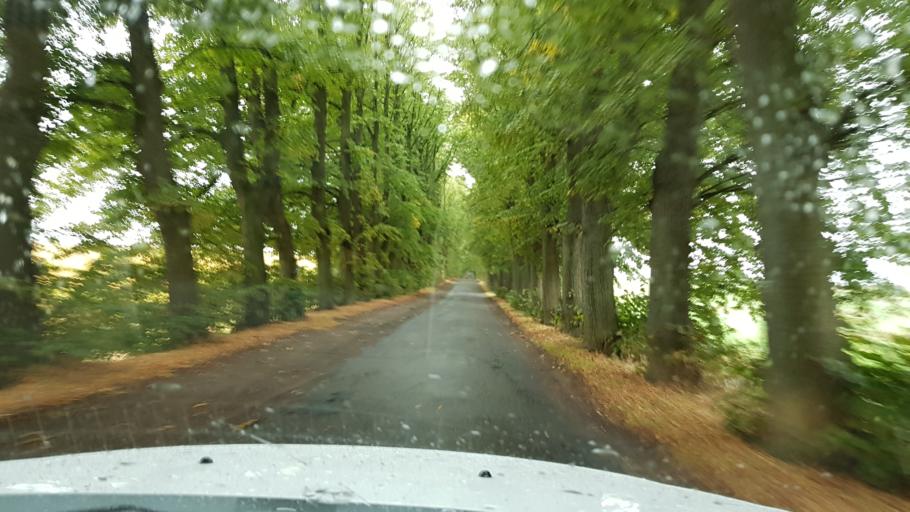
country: DE
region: Brandenburg
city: Schwedt (Oder)
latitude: 53.0134
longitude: 14.3058
